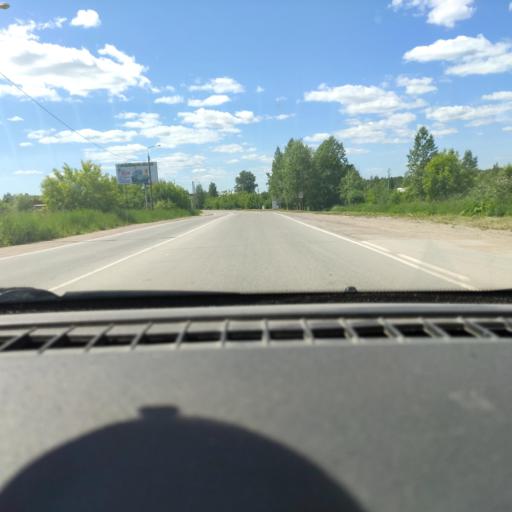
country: RU
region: Perm
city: Krasnokamsk
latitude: 58.0779
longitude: 55.7044
